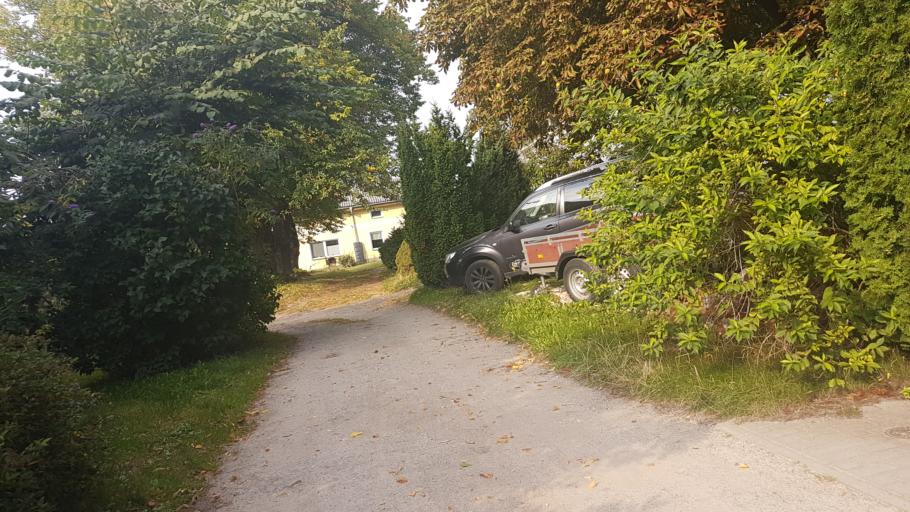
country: DE
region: Mecklenburg-Vorpommern
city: Garz
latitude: 54.3062
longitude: 13.3534
